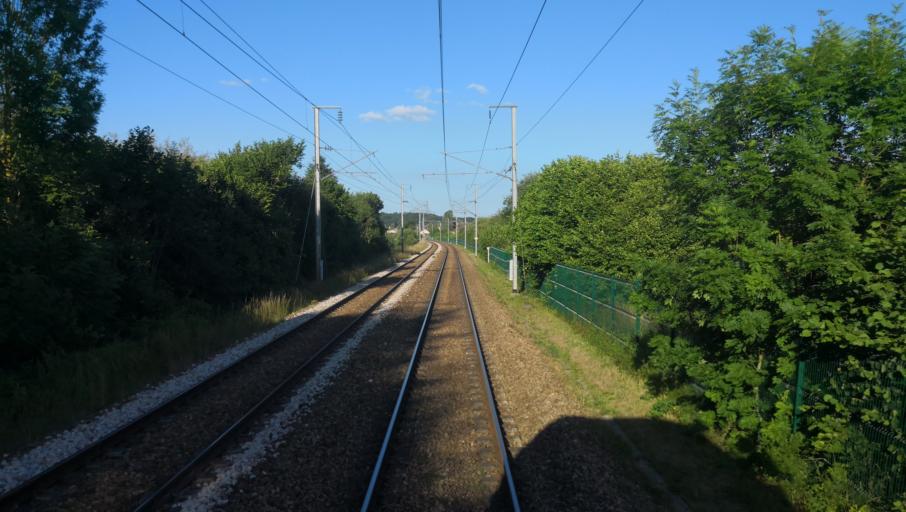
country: FR
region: Haute-Normandie
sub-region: Departement de l'Eure
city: Saint-Sebastien-de-Morsent
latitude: 48.9944
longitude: 1.0858
